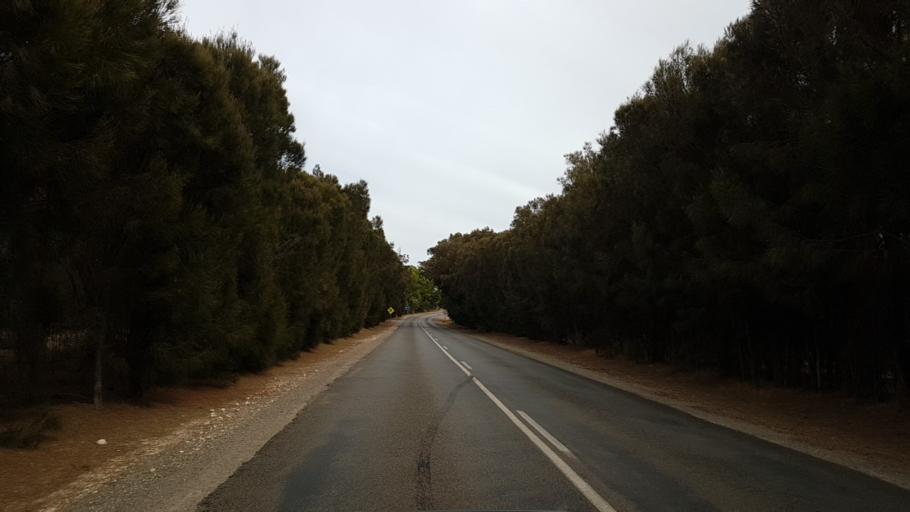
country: AU
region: South Australia
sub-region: Yorke Peninsula
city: Port Victoria
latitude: -34.7729
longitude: 137.6028
